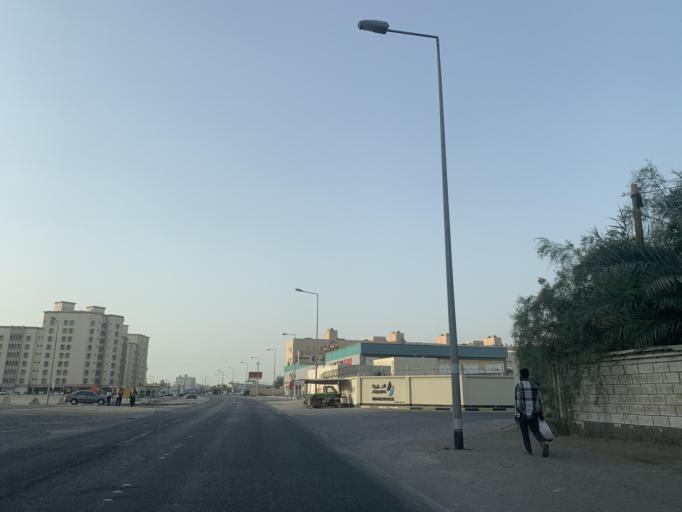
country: BH
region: Northern
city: Madinat `Isa
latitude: 26.1882
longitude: 50.5572
